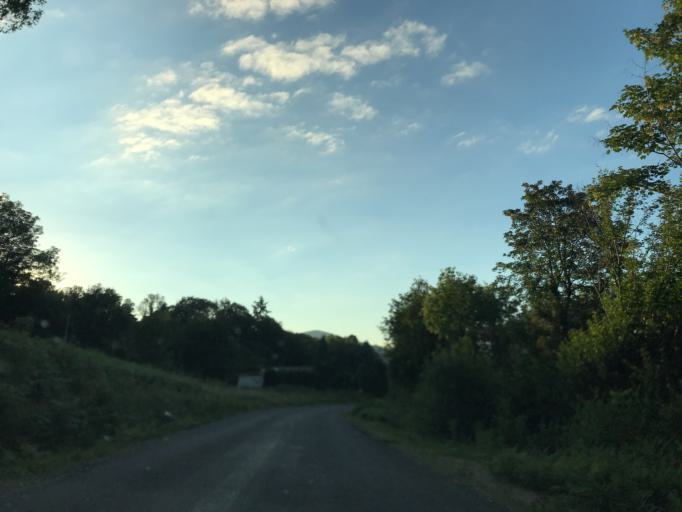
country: FR
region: Rhone-Alpes
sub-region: Departement de la Loire
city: Noiretable
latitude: 45.7949
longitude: 3.7708
